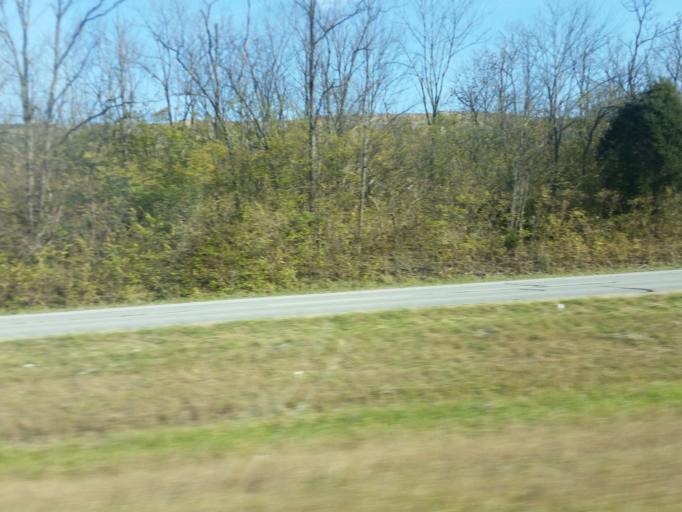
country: US
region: Ohio
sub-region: Hamilton County
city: Dunlap
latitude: 39.2753
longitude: -84.6042
